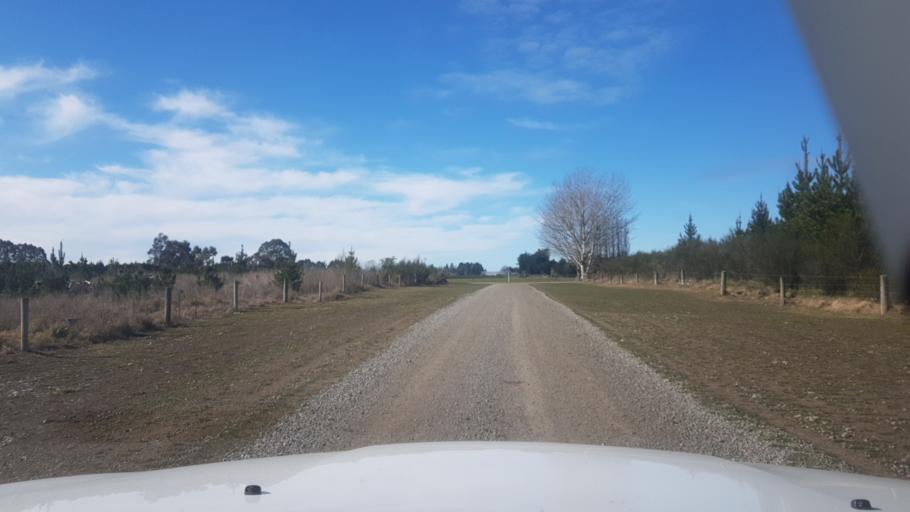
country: NZ
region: Canterbury
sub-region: Timaru District
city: Pleasant Point
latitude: -44.1371
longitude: 171.2754
